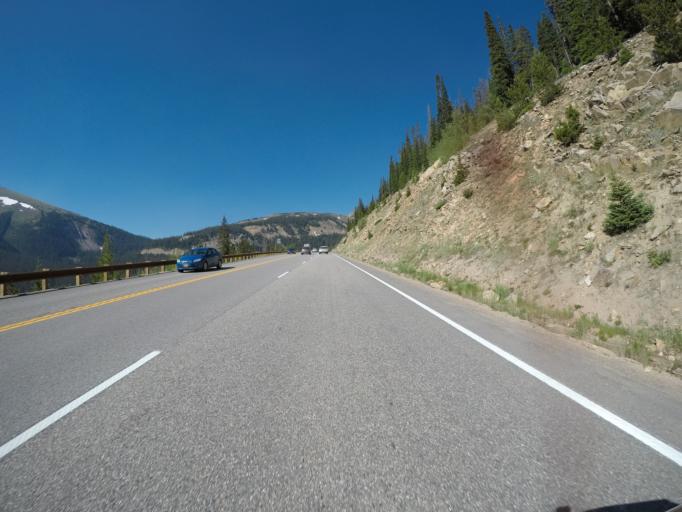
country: US
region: Colorado
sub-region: Clear Creek County
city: Georgetown
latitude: 39.8164
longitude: -105.7704
